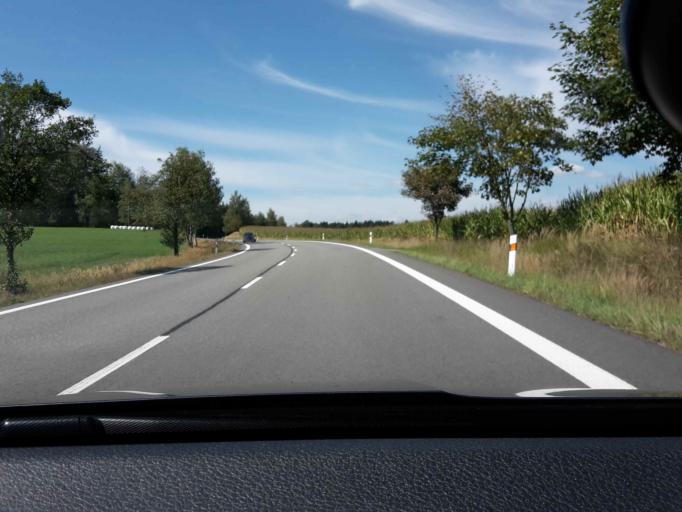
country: CZ
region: Jihocesky
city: Strmilov
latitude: 49.1780
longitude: 15.1491
